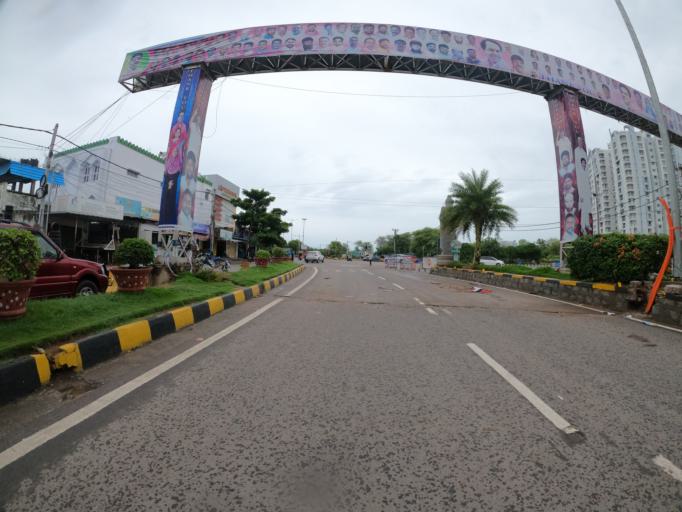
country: IN
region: Telangana
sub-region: Rangareddi
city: Kukatpalli
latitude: 17.4647
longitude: 78.3757
